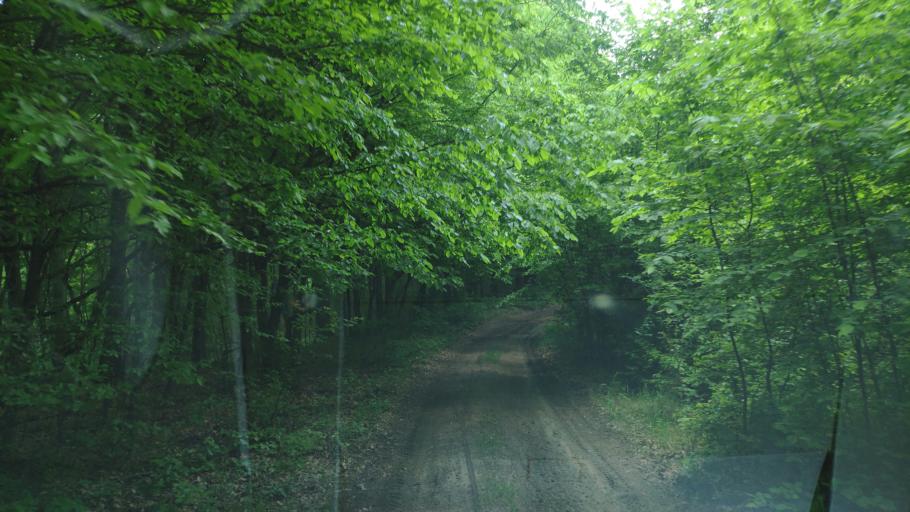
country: SK
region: Presovsky
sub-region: Okres Presov
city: Presov
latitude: 48.9406
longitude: 21.1182
